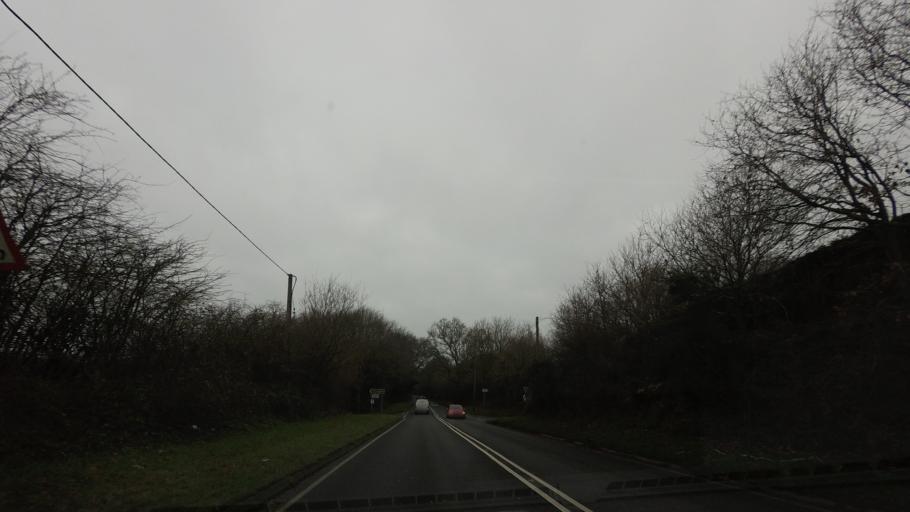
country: GB
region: England
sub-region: East Sussex
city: Battle
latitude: 50.9415
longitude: 0.5134
